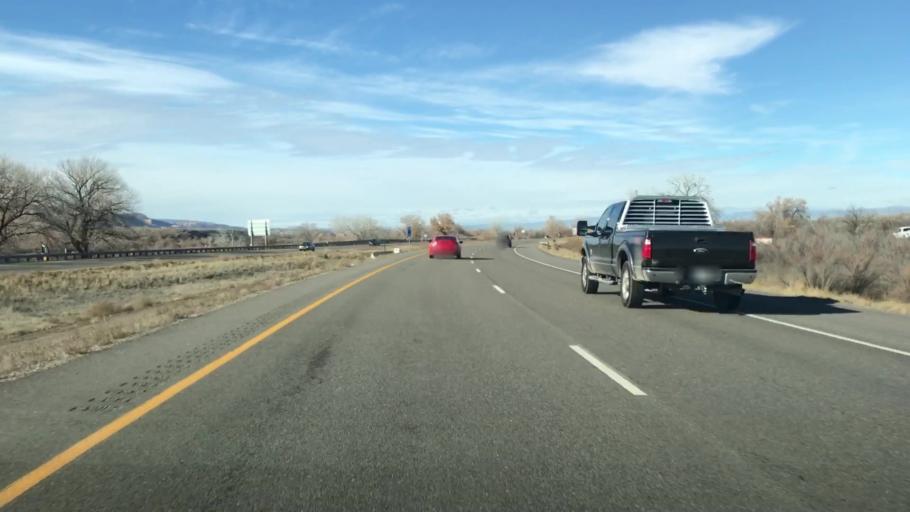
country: US
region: Colorado
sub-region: Mesa County
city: Redlands
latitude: 39.1103
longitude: -108.6583
